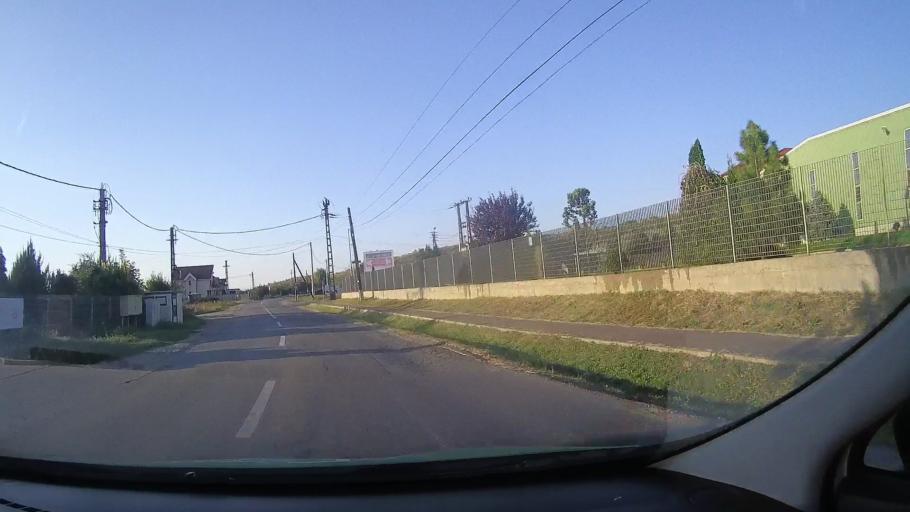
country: RO
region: Bihor
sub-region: Comuna Biharea
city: Oradea
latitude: 47.0937
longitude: 21.9249
